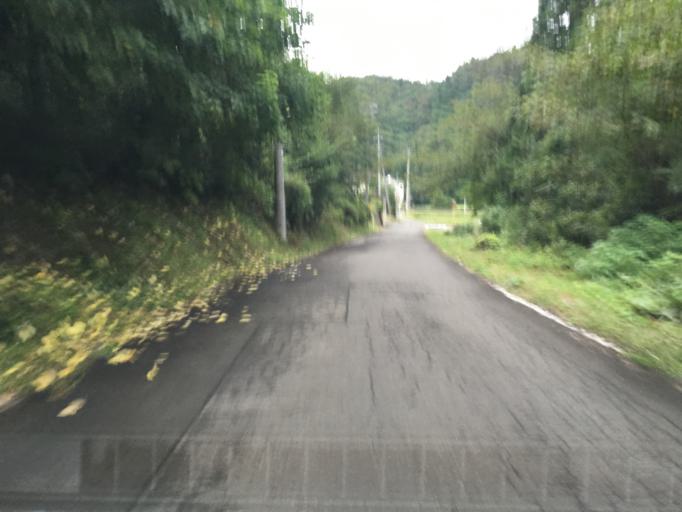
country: JP
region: Fukushima
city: Hobaramachi
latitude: 37.7568
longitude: 140.5445
